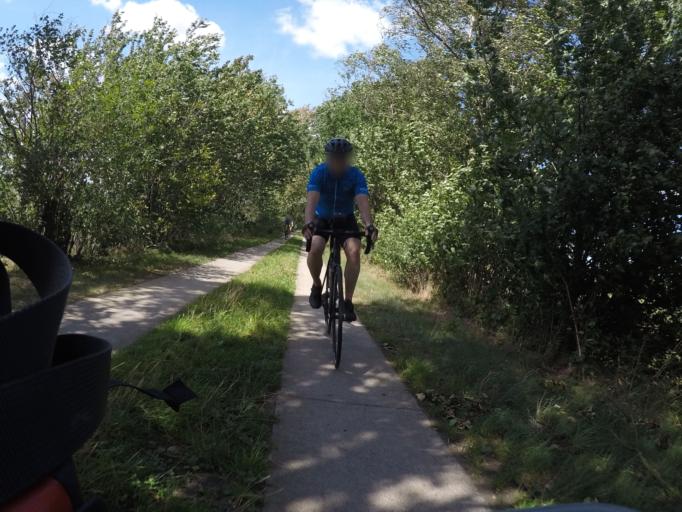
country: DE
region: Lower Saxony
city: Stelle
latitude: 53.4520
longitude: 10.1236
